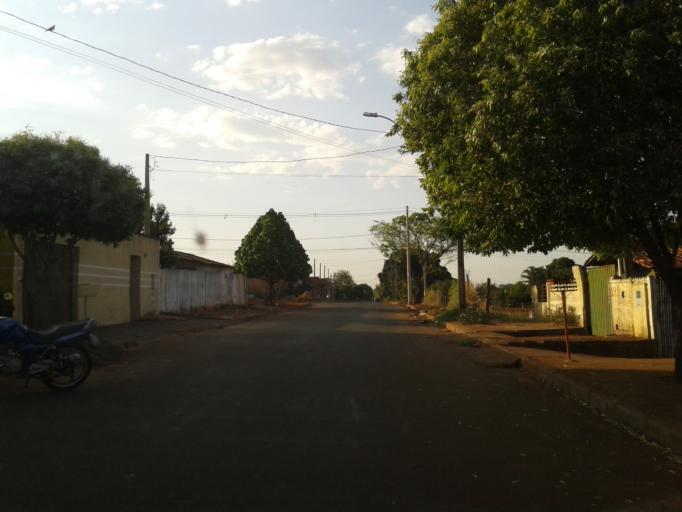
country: BR
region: Minas Gerais
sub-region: Ituiutaba
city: Ituiutaba
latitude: -18.9906
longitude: -49.4427
